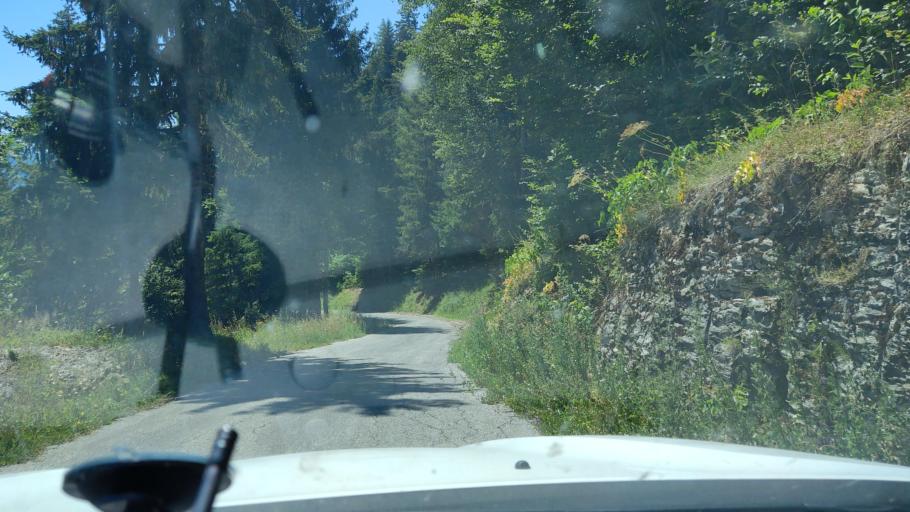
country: FR
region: Rhone-Alpes
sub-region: Departement de la Savoie
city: Salins-les-Thermes
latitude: 45.4687
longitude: 6.5067
